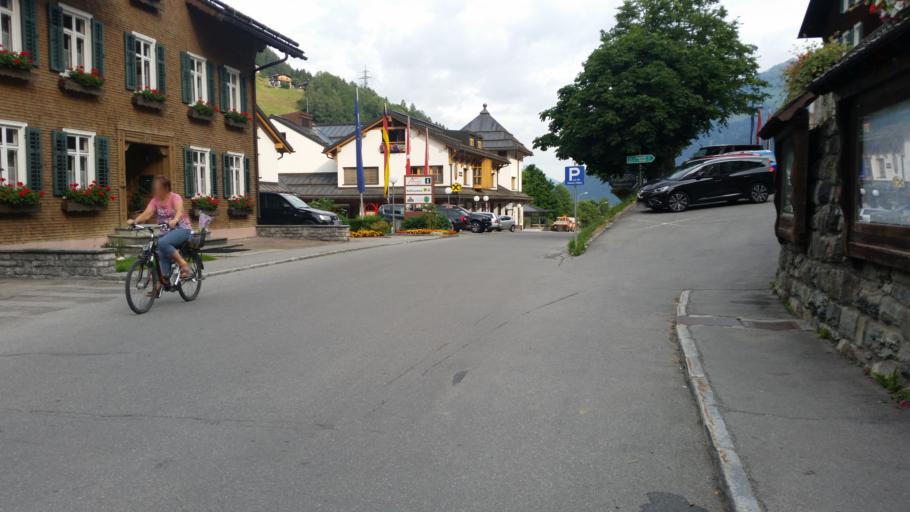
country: AT
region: Vorarlberg
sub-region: Politischer Bezirk Bludenz
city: Gaschurn
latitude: 46.9875
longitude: 10.0264
